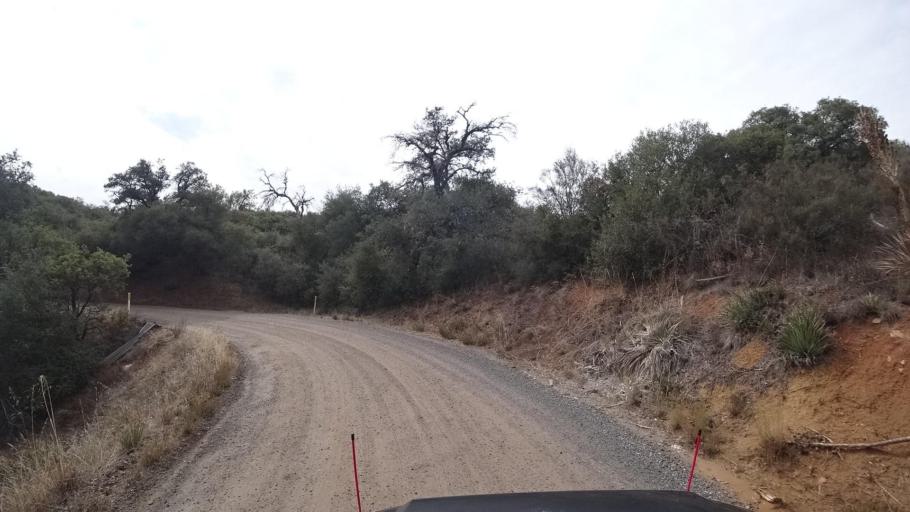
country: US
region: California
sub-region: San Diego County
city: Descanso
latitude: 32.8588
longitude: -116.6207
